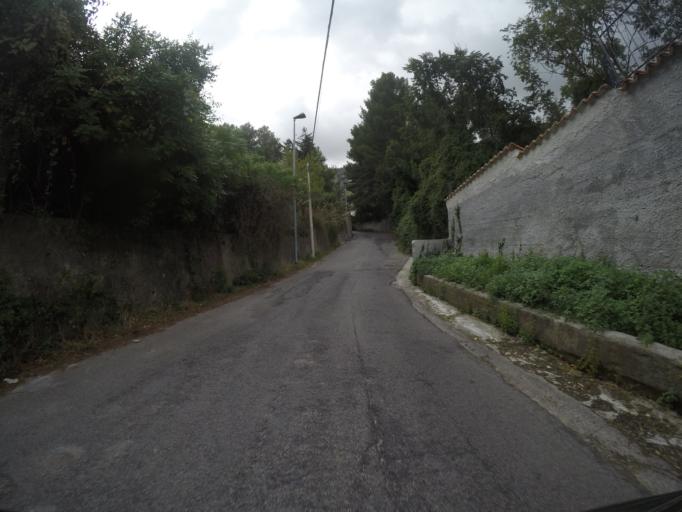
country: IT
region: Sicily
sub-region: Palermo
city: Carini
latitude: 38.1247
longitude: 13.1831
